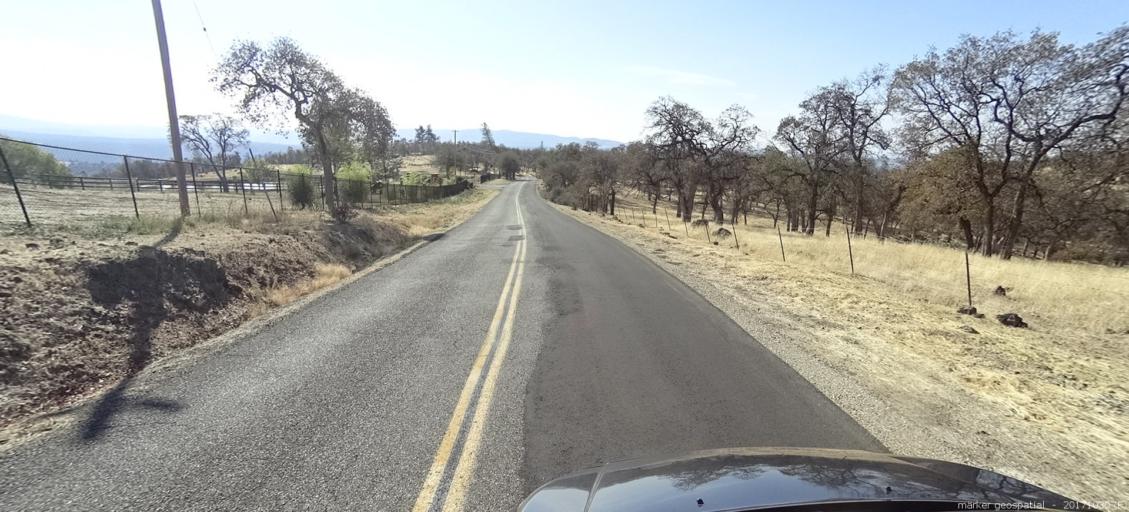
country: US
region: California
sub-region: Shasta County
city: Shingletown
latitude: 40.6641
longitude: -121.9485
